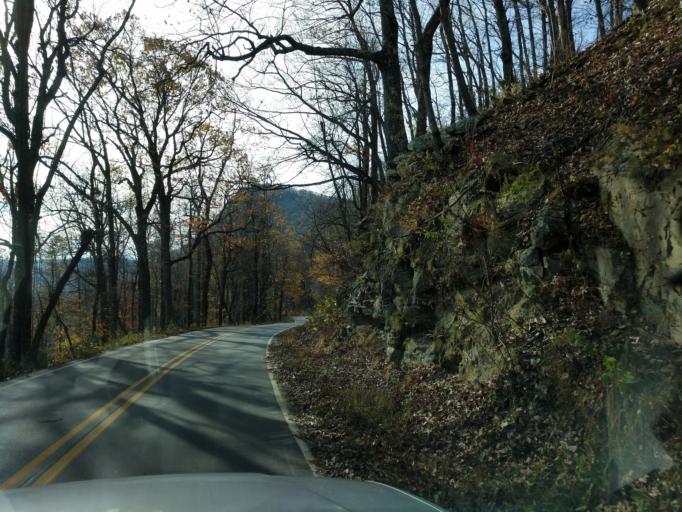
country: US
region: North Carolina
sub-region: Polk County
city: Columbus
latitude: 35.2703
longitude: -82.2289
